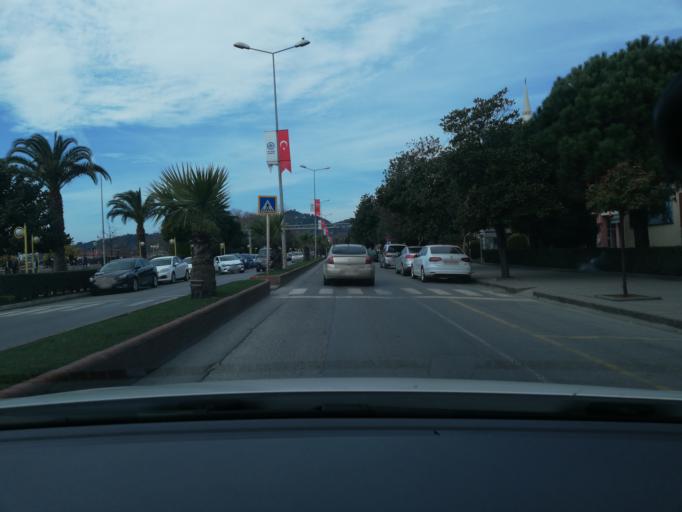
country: TR
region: Zonguldak
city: Eregli
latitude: 41.2825
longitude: 31.4155
